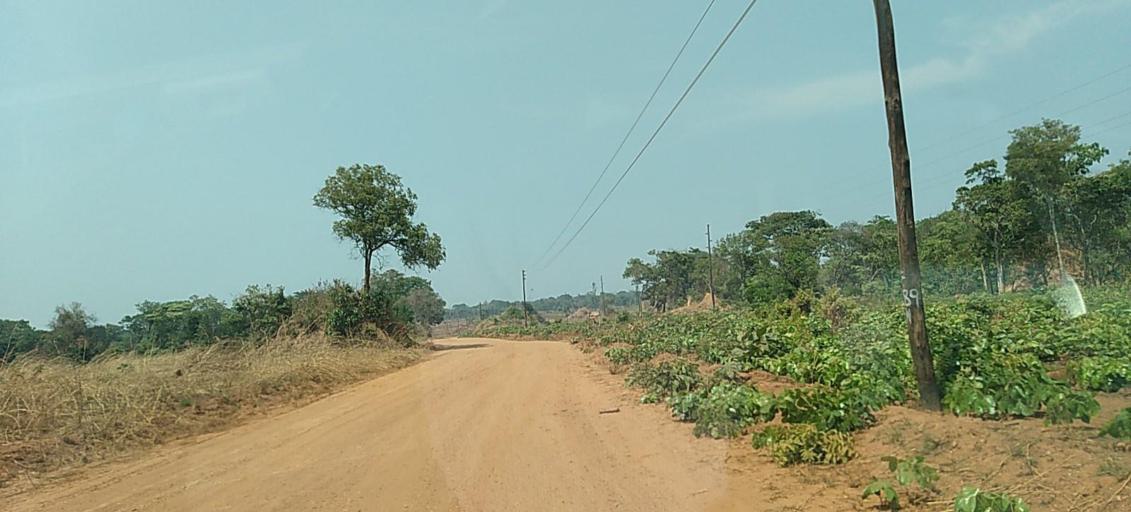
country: ZM
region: Copperbelt
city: Chingola
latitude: -13.0615
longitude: 27.4201
